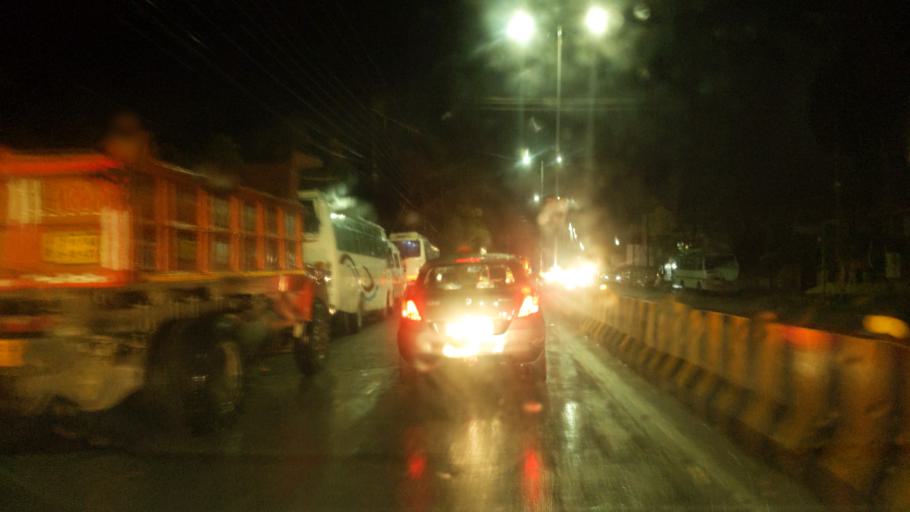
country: IN
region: Uttarakhand
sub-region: Naini Tal
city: Haldwani
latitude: 29.2509
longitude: 79.5407
